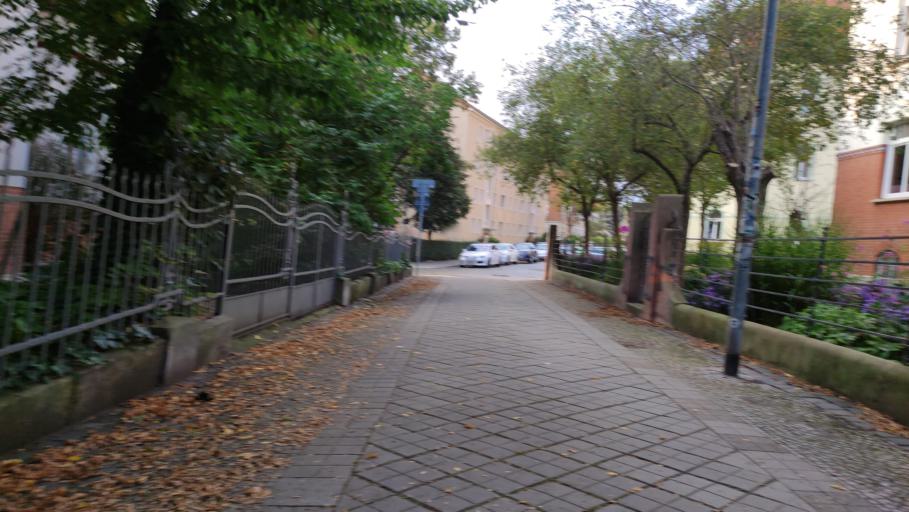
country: DE
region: Thuringia
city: Erfurt
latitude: 50.9680
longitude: 11.0228
